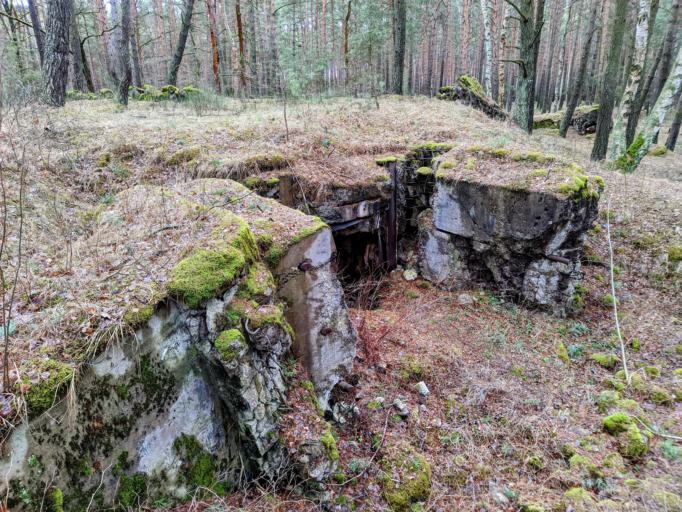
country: PL
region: Lubusz
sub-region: Powiat swiebodzinski
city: Skape
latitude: 52.1657
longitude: 15.4320
